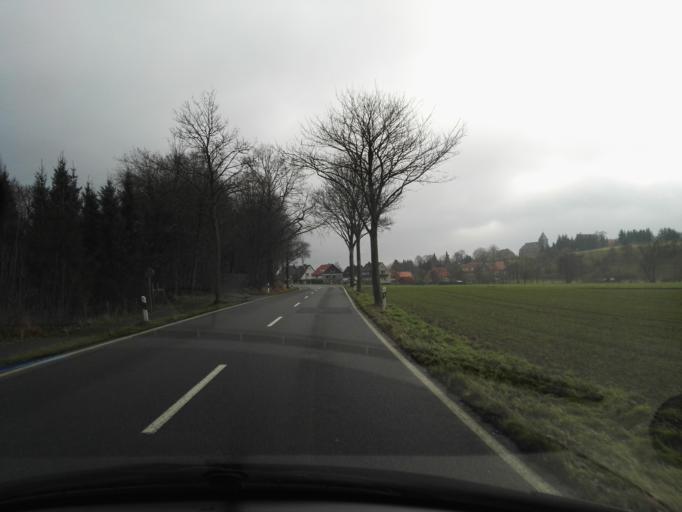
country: DE
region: Lower Saxony
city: Eberholzen
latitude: 52.0782
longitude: 9.8618
